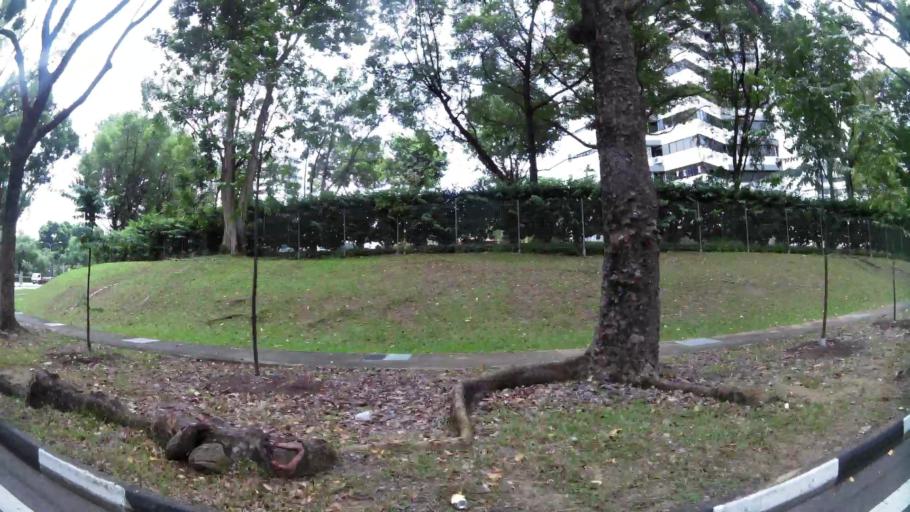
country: SG
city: Singapore
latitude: 1.3155
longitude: 103.7602
